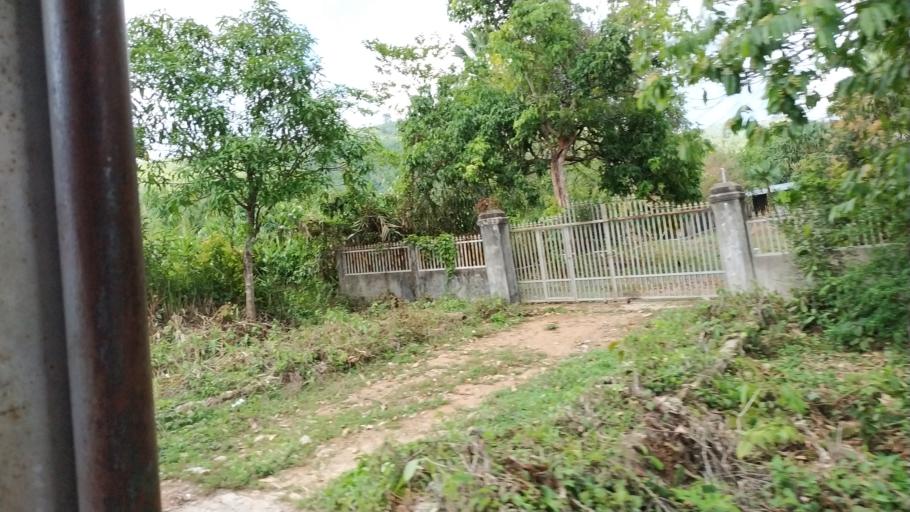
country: MM
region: Mon
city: Kyaikto
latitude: 17.4091
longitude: 97.0731
